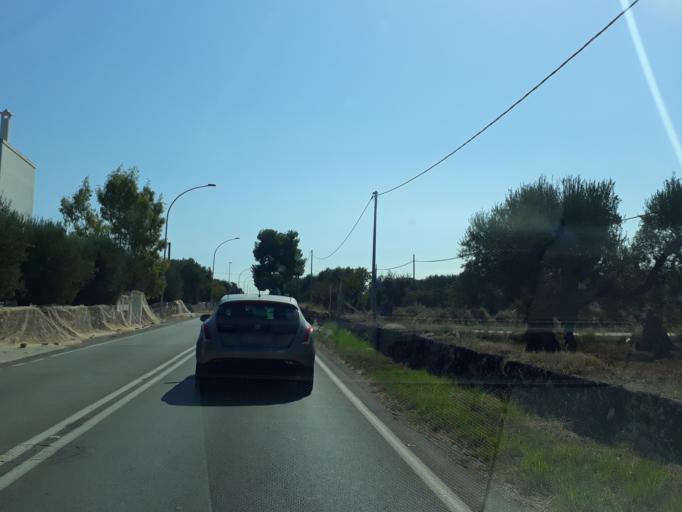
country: IT
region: Apulia
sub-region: Provincia di Bari
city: Monopoli
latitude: 40.9322
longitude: 17.3111
